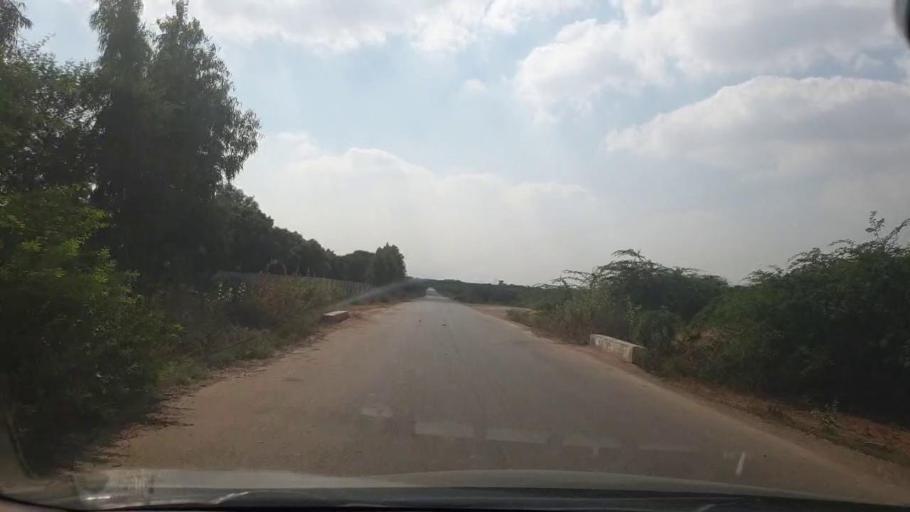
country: PK
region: Sindh
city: Malir Cantonment
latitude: 25.0204
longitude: 67.3546
